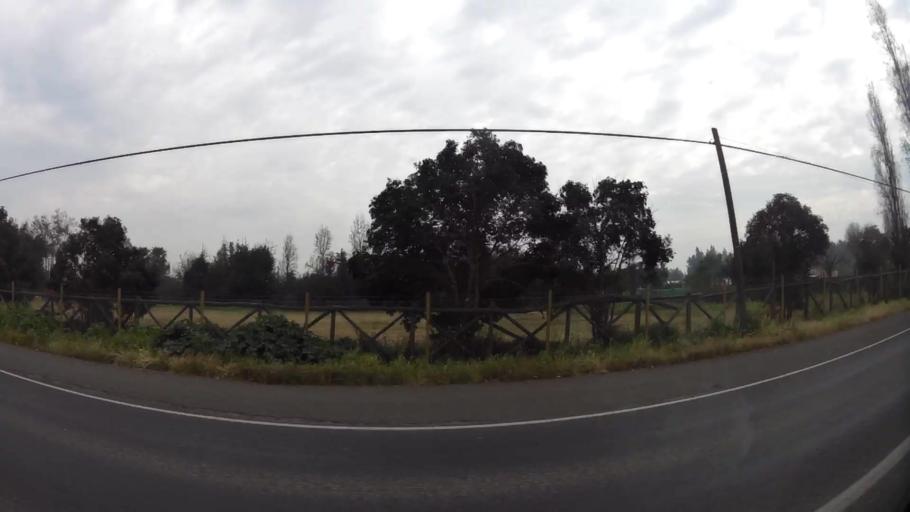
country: CL
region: Santiago Metropolitan
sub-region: Provincia de Chacabuco
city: Chicureo Abajo
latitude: -33.2477
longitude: -70.7119
